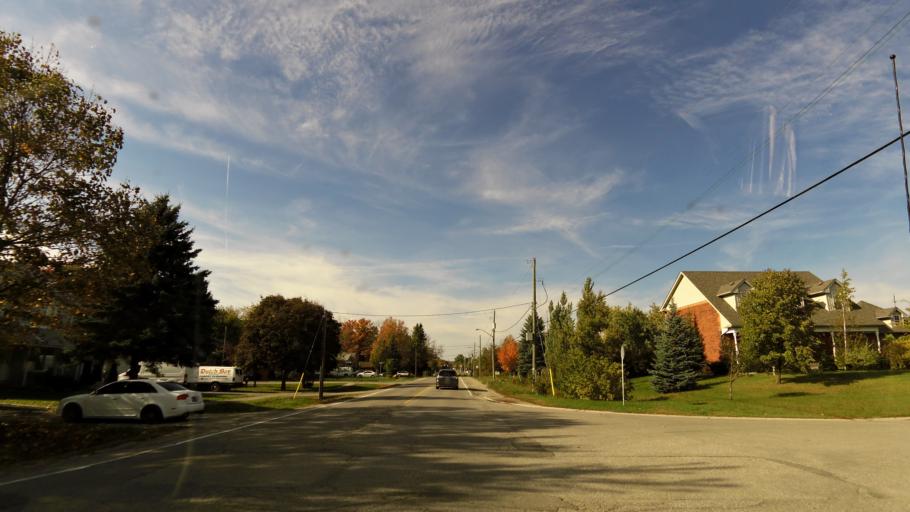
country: CA
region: Ontario
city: Orangeville
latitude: 43.7636
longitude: -80.0550
